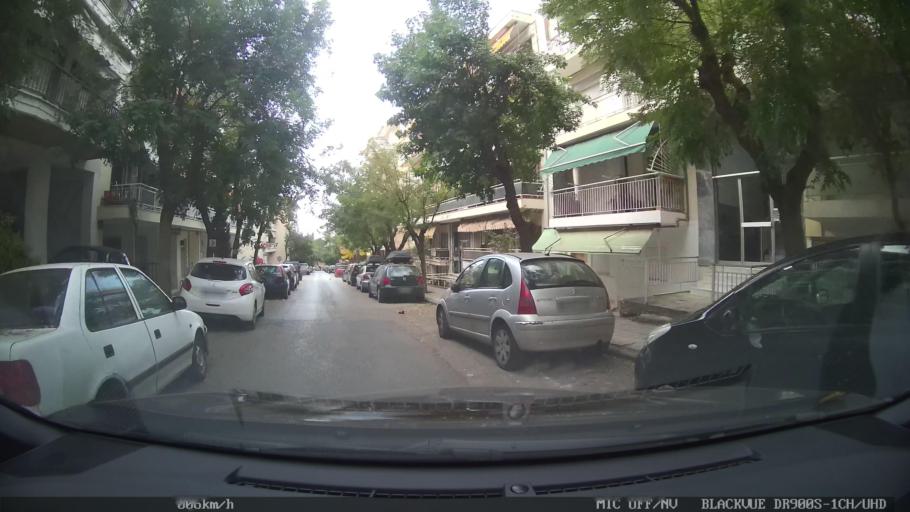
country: GR
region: Central Macedonia
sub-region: Nomos Thessalonikis
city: Triandria
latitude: 40.6151
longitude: 22.9816
